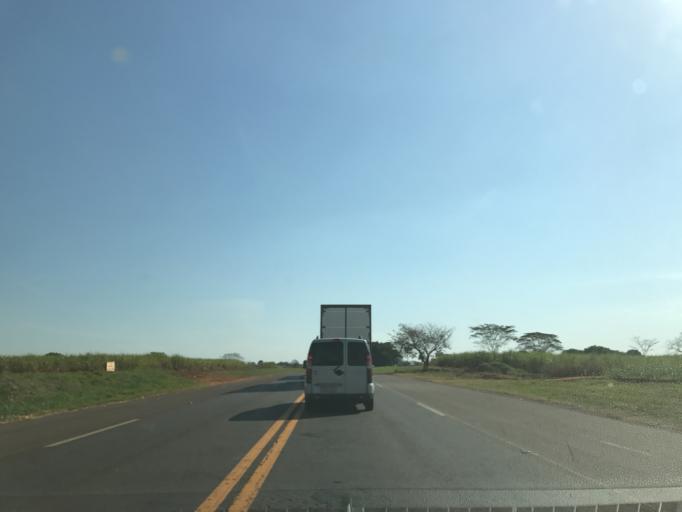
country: BR
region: Sao Paulo
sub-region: Penapolis
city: Penapolis
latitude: -21.4861
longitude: -50.2144
